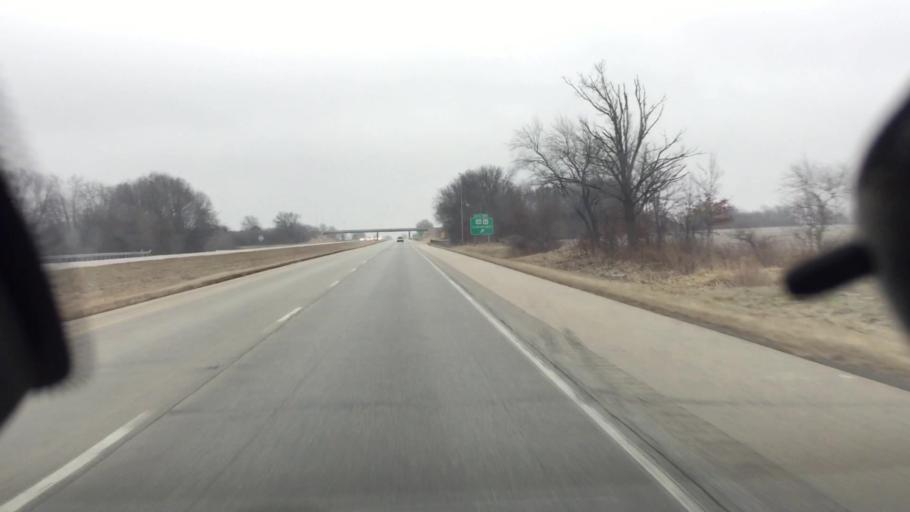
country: US
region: Illinois
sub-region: Knox County
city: Knoxville
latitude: 40.9154
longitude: -90.2528
